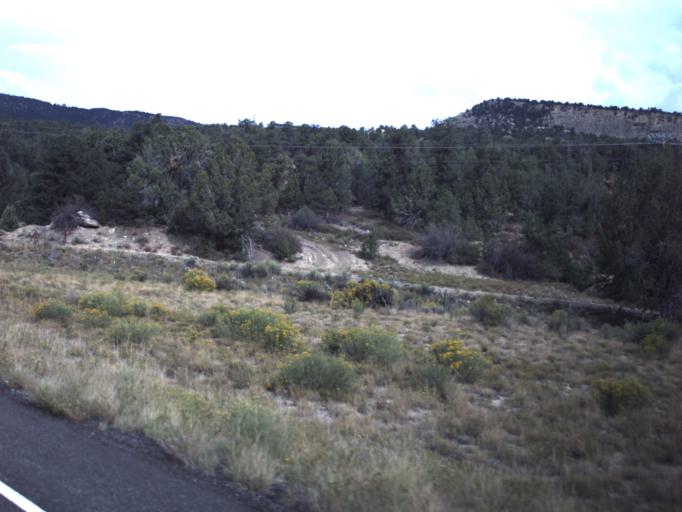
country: US
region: Utah
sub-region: Washington County
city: Hildale
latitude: 37.2629
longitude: -112.7741
